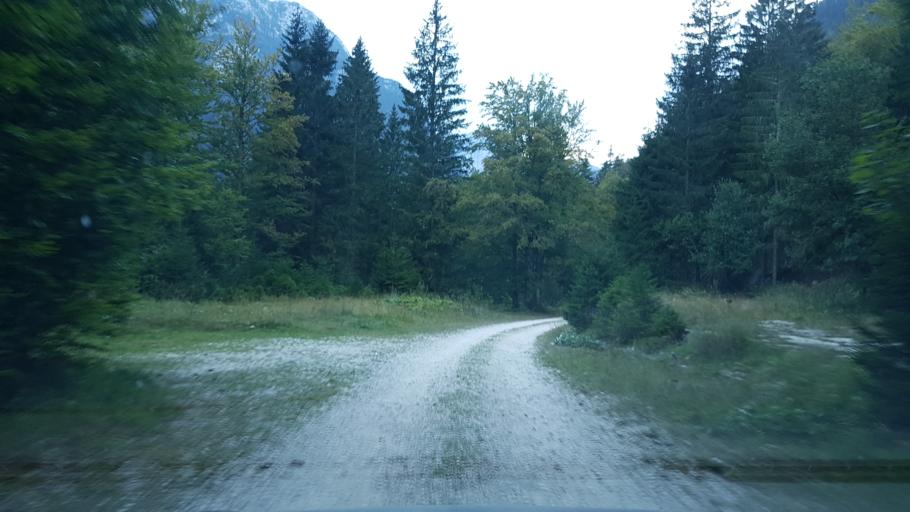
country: SI
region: Bovec
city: Bovec
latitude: 46.4020
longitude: 13.5090
